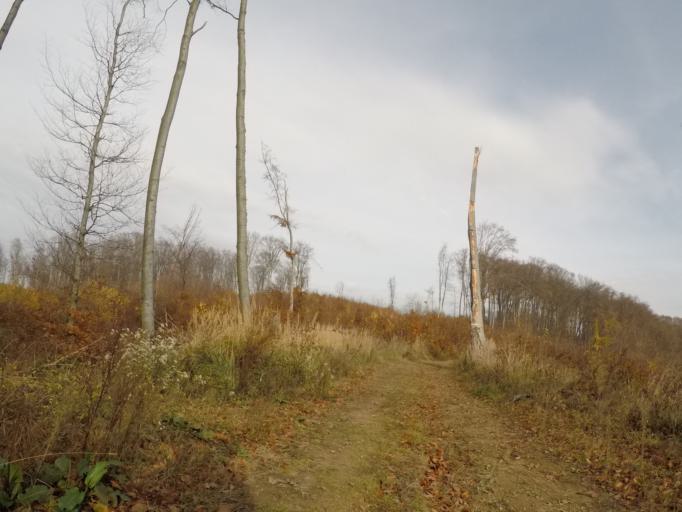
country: SK
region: Presovsky
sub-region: Okres Presov
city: Presov
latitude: 48.9562
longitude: 21.2099
